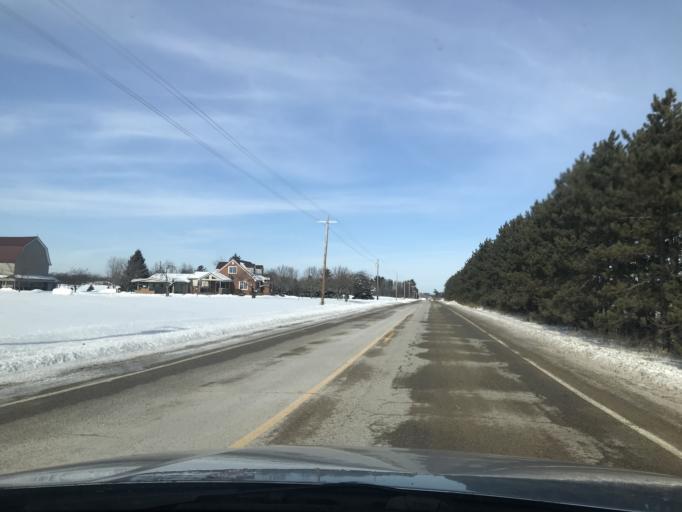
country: US
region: Wisconsin
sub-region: Oconto County
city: Oconto Falls
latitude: 45.1158
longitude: -88.1783
